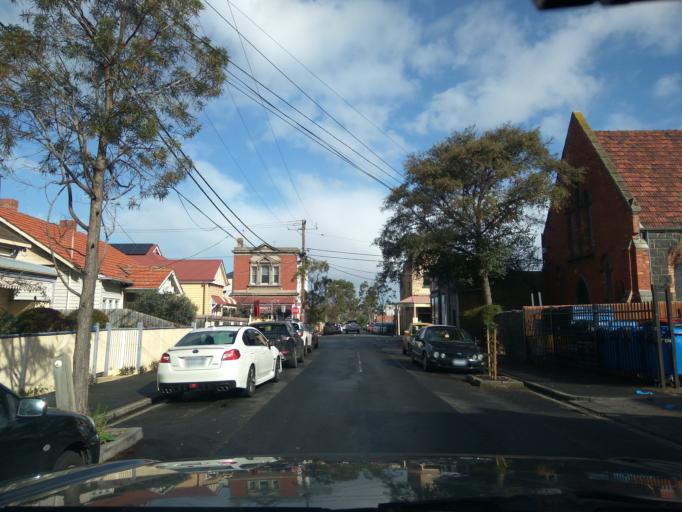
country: AU
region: Victoria
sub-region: Maribyrnong
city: Yarraville
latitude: -37.8172
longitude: 144.8913
